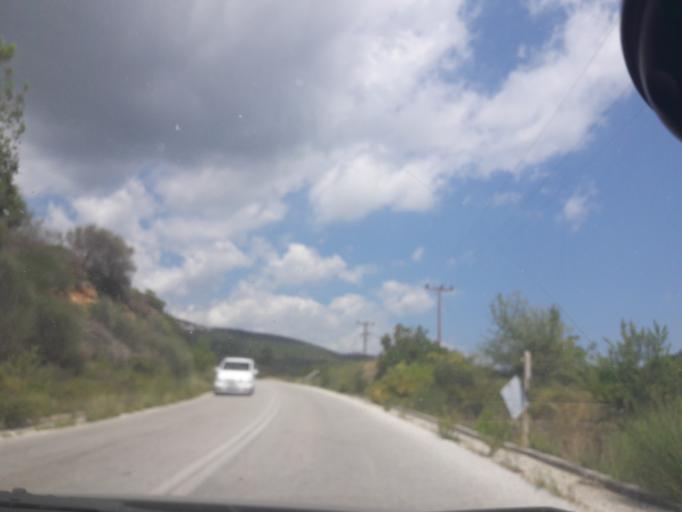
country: GR
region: Central Macedonia
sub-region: Nomos Chalkidikis
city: Polygyros
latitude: 40.3724
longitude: 23.5160
